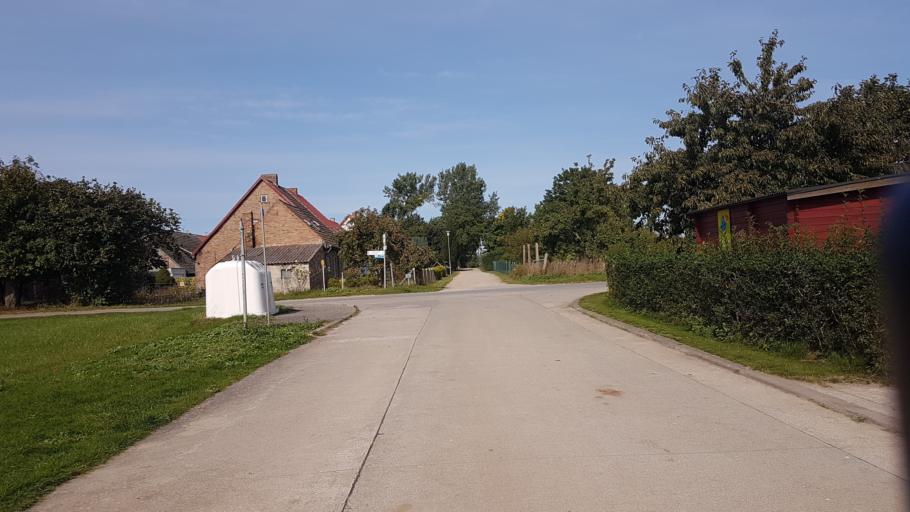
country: DE
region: Mecklenburg-Vorpommern
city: Gingst
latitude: 54.4190
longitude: 13.2552
